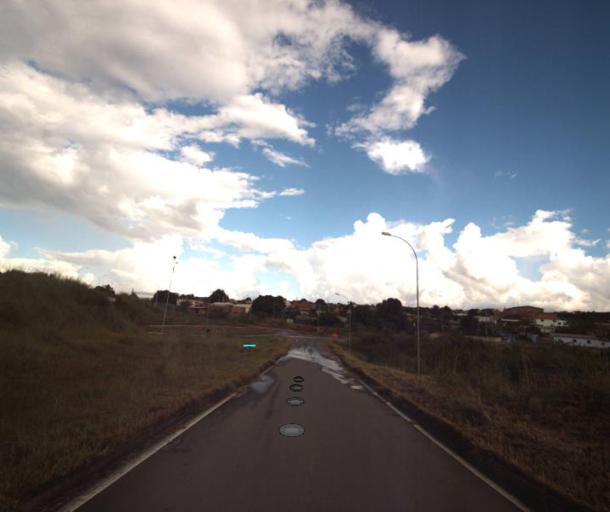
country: BR
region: Goias
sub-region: Anapolis
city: Anapolis
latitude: -16.2718
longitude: -48.9743
